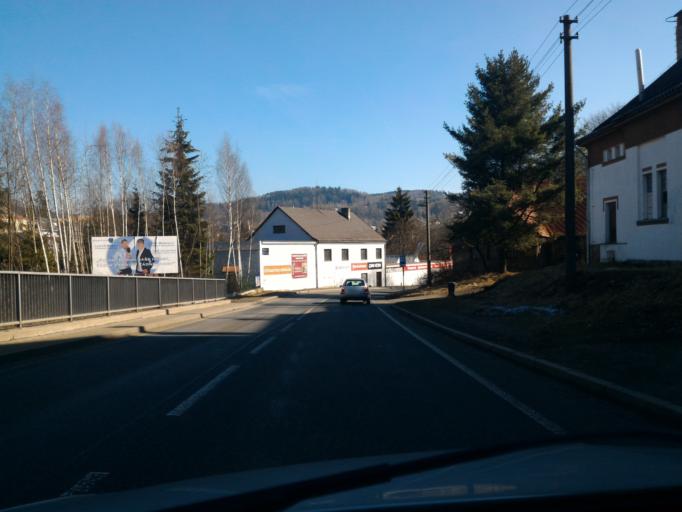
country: CZ
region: Liberecky
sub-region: Okres Jablonec nad Nisou
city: Tanvald
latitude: 50.7350
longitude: 15.3026
